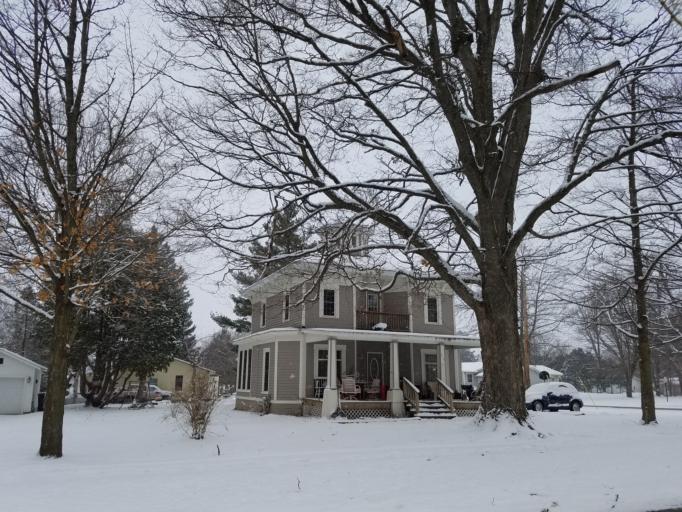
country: US
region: Michigan
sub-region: Barry County
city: Nashville
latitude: 42.6251
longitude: -85.0249
